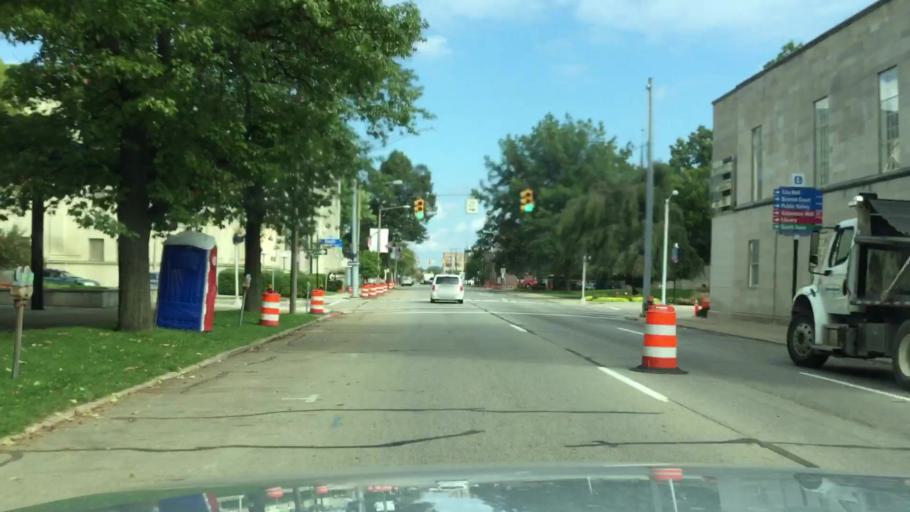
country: US
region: Michigan
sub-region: Kalamazoo County
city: Kalamazoo
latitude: 42.2892
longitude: -85.5873
